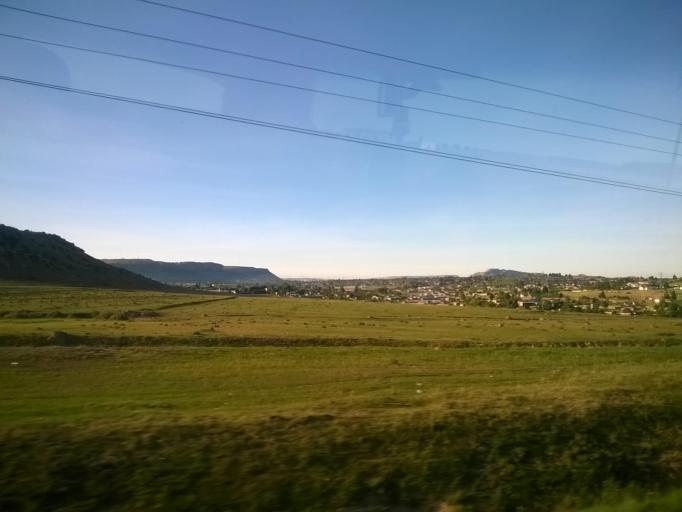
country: LS
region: Maseru
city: Maseru
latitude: -29.2647
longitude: 27.5564
